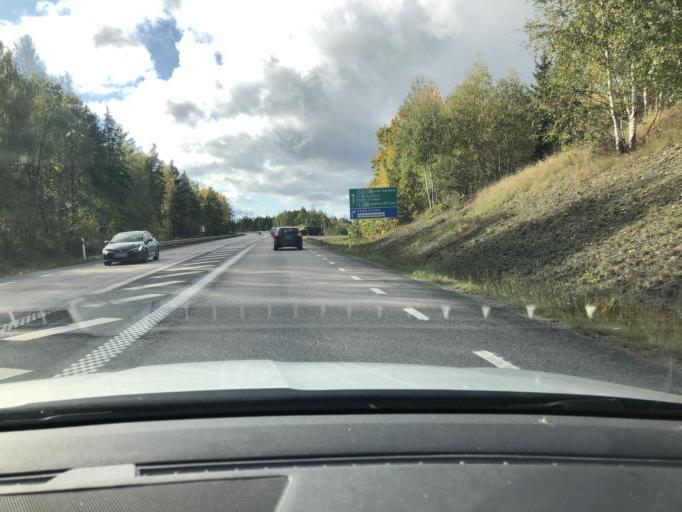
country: SE
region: Soedermanland
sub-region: Strangnas Kommun
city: Strangnas
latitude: 59.3768
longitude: 16.9744
